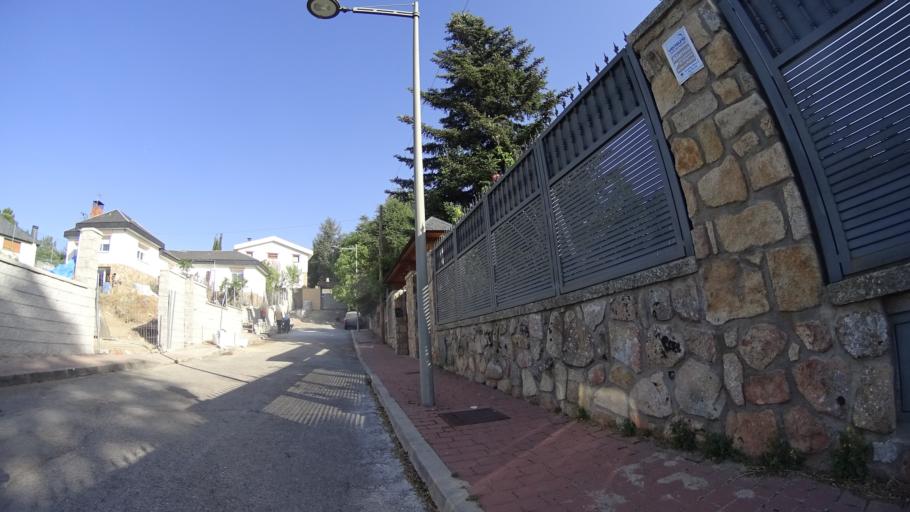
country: ES
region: Madrid
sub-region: Provincia de Madrid
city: Guadarrama
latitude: 40.6803
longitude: -4.1024
